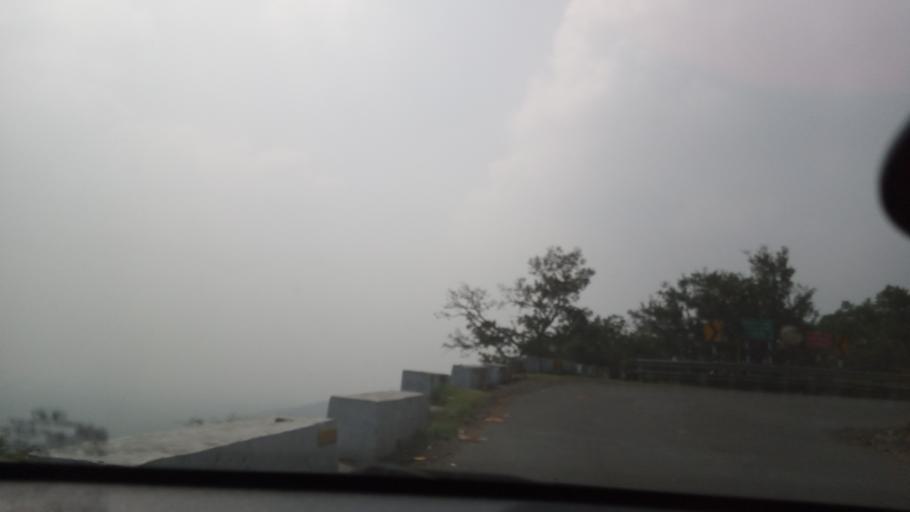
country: IN
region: Tamil Nadu
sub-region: Erode
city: Sathyamangalam
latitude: 11.5924
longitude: 77.1271
